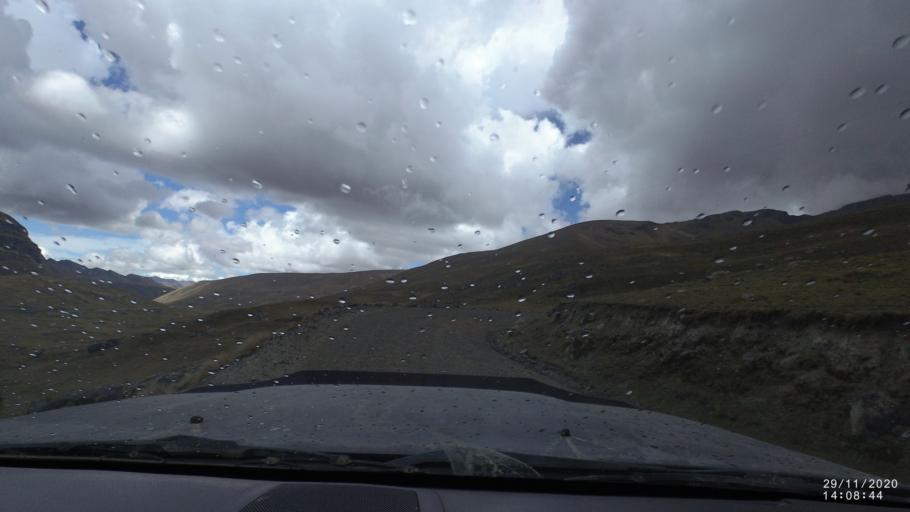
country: BO
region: Cochabamba
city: Sipe Sipe
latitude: -17.2240
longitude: -66.3831
